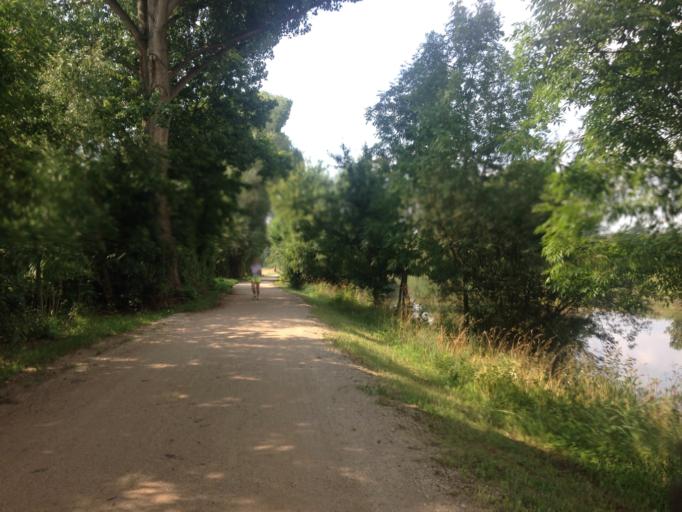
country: DE
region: Hesse
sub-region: Regierungsbezirk Darmstadt
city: Frankfurt am Main
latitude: 50.1694
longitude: 8.6518
